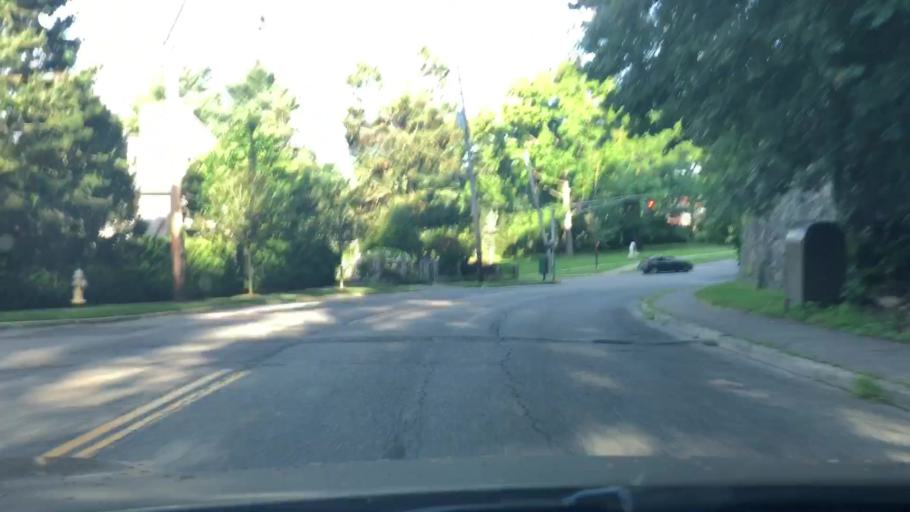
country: US
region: New York
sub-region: Westchester County
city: Bronxville
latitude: 40.9345
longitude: -73.8295
